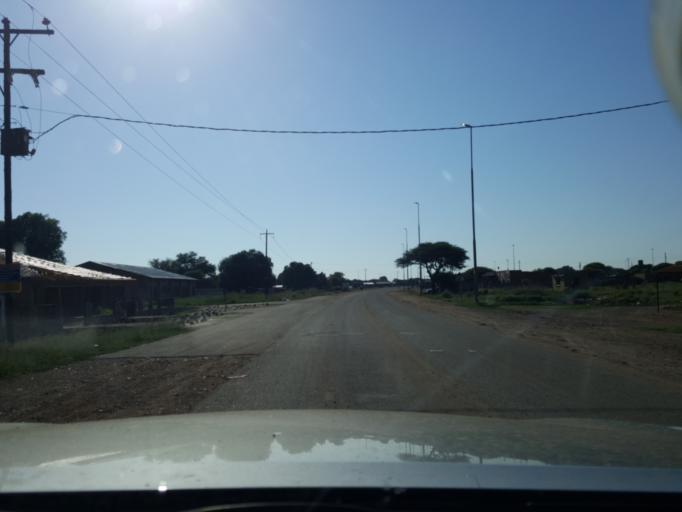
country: ZA
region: North-West
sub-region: Ngaka Modiri Molema District Municipality
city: Mmabatho
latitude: -25.8261
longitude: 25.6439
